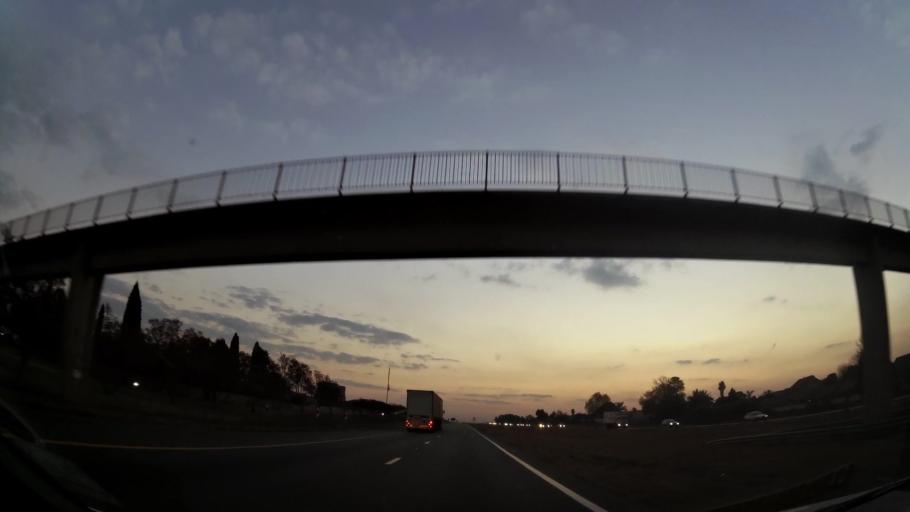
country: ZA
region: Gauteng
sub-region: Ekurhuleni Metropolitan Municipality
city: Boksburg
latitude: -26.2518
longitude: 28.2587
